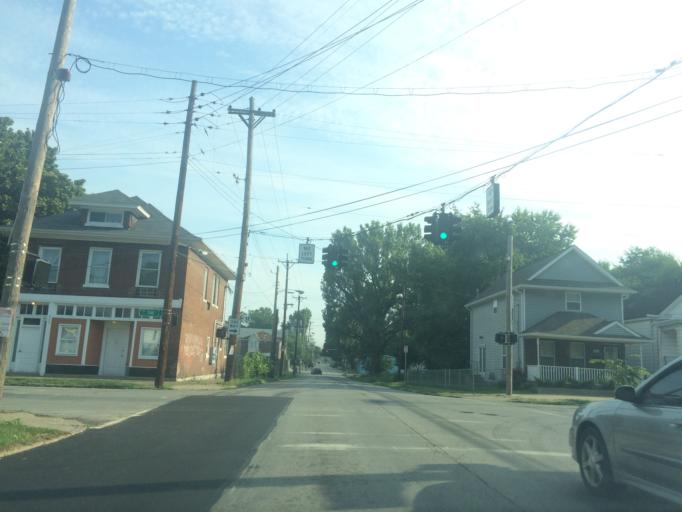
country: US
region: Kentucky
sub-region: Jefferson County
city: Louisville
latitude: 38.2340
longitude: -85.7476
